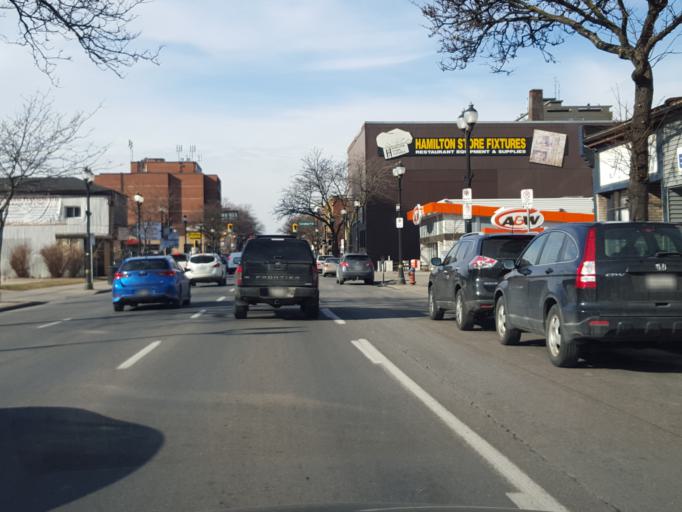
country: CA
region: Ontario
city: Hamilton
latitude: 43.2581
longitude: -79.8744
